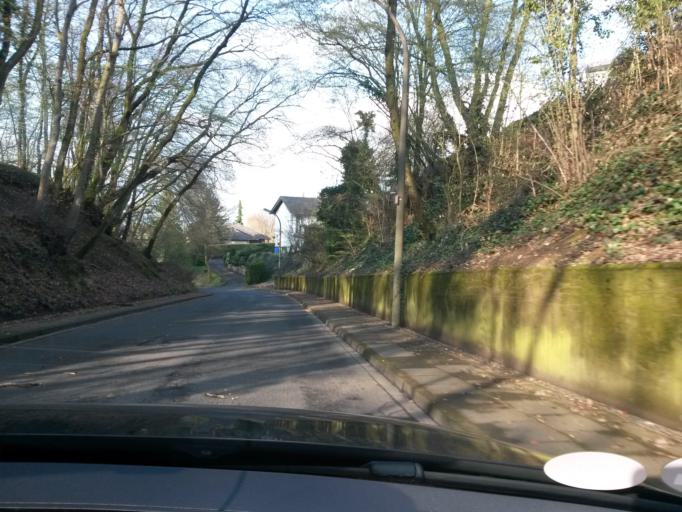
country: DE
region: North Rhine-Westphalia
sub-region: Regierungsbezirk Koln
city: Alfter
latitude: 50.7086
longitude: 7.0377
